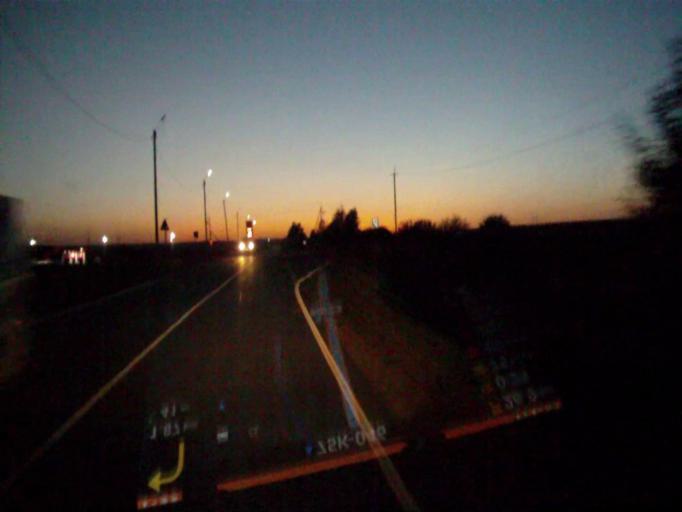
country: RU
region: Chelyabinsk
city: Chebarkul'
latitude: 55.2227
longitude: 60.4785
